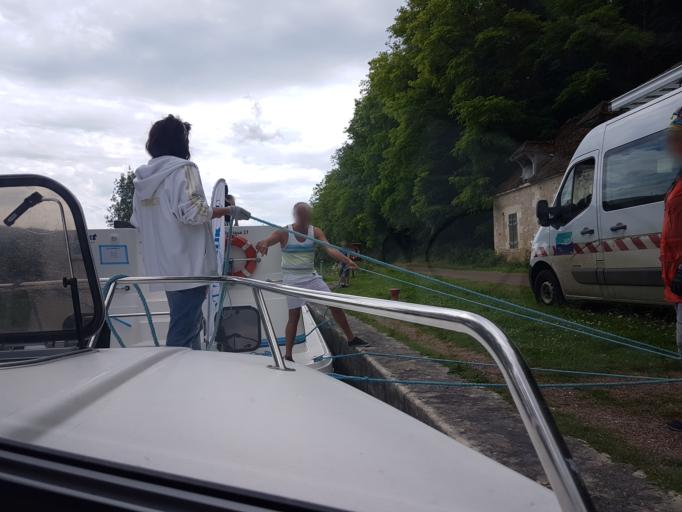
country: FR
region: Bourgogne
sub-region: Departement de la Nievre
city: Clamecy
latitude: 47.4873
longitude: 3.5244
